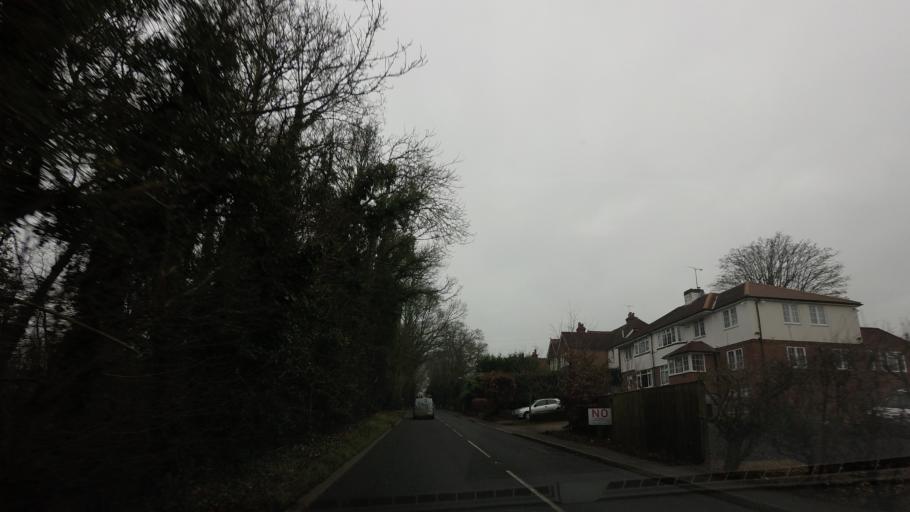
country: GB
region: England
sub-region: Kent
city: Hawkhurst
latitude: 51.0554
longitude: 0.5069
